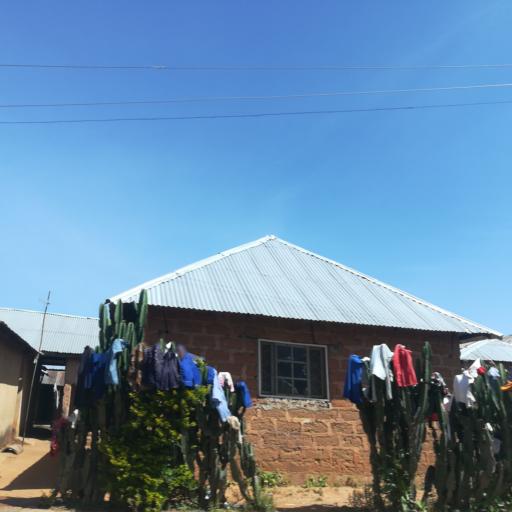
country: NG
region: Plateau
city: Bukuru
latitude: 9.7583
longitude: 8.8678
